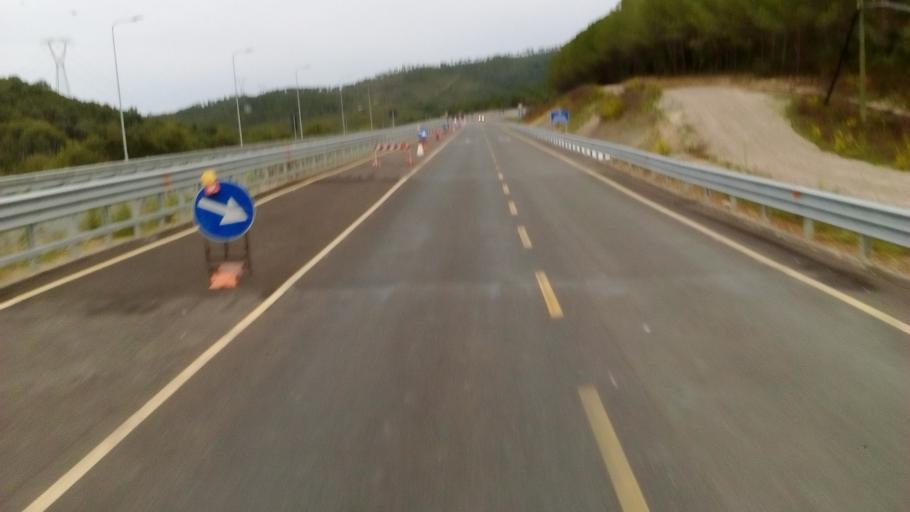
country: IT
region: Tuscany
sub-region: Provincia di Grosseto
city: Civitella Marittima
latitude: 43.0298
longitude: 11.2776
